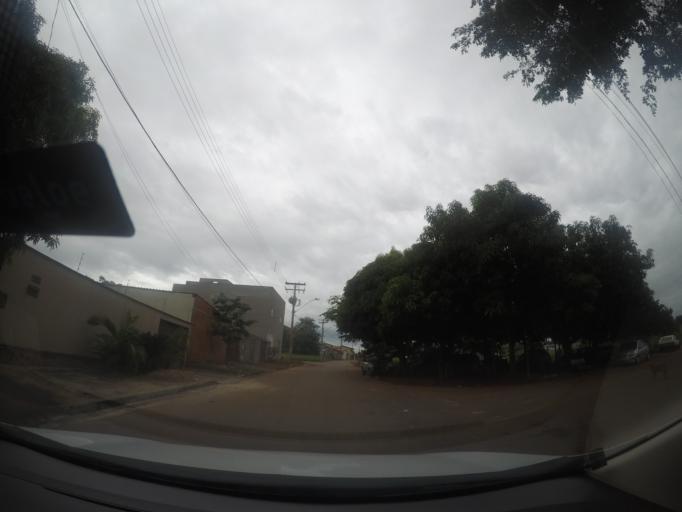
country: BR
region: Goias
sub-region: Goiania
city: Goiania
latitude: -16.6142
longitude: -49.3089
